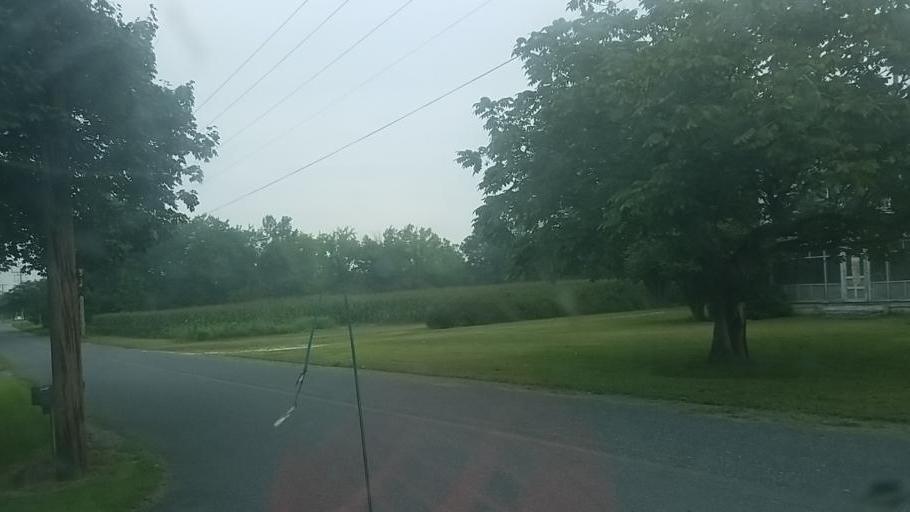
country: US
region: Maryland
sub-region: Wicomico County
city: Salisbury
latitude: 38.3646
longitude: -75.5404
